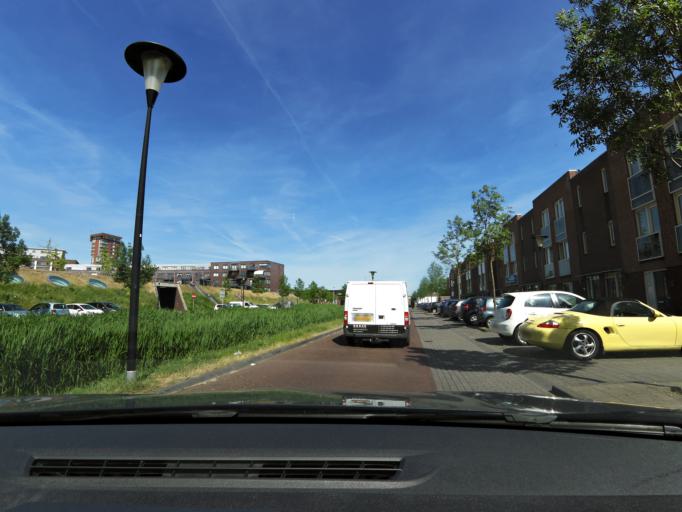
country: NL
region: South Holland
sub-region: Gemeente Binnenmaas
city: Heinenoord
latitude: 51.8463
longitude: 4.4984
